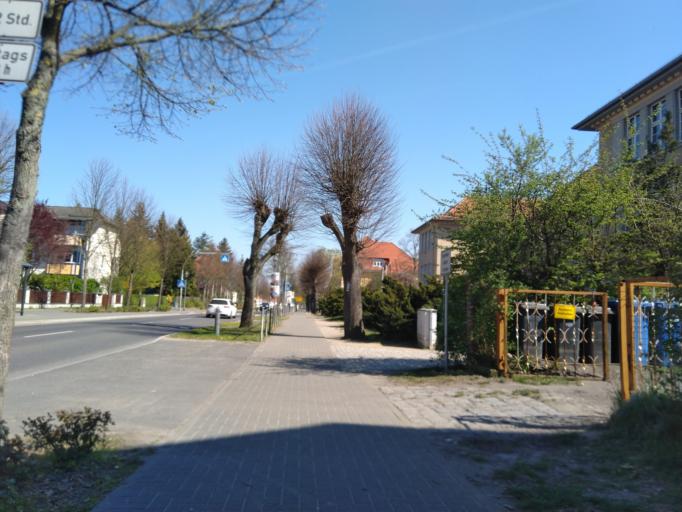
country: DE
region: Brandenburg
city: Biesenthal
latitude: 52.7663
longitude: 13.6398
